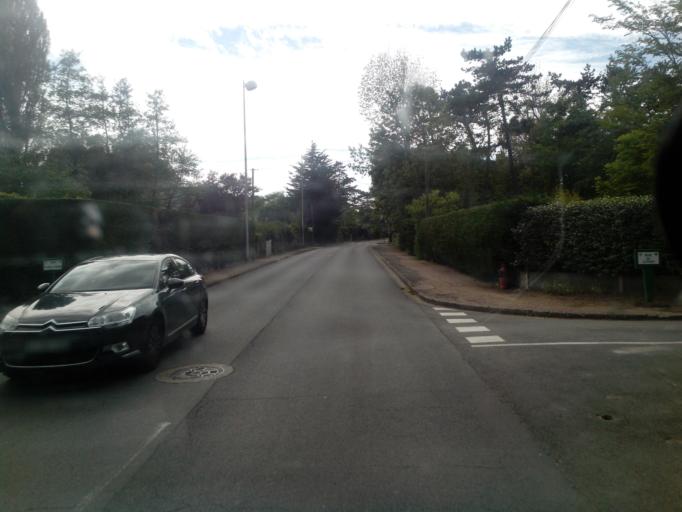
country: FR
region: Lower Normandy
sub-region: Departement du Calvados
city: Merville-Franceville-Plage
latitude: 49.2846
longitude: -0.1640
